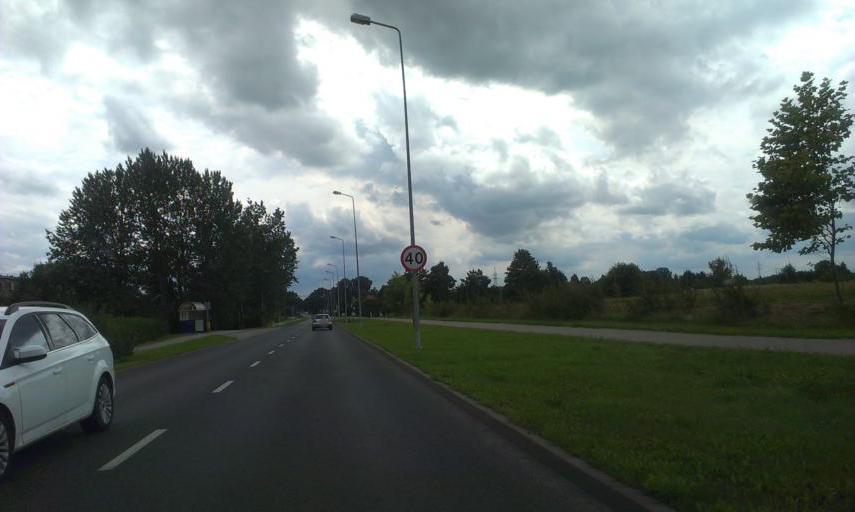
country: PL
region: West Pomeranian Voivodeship
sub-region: Koszalin
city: Koszalin
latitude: 54.1744
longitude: 16.1845
